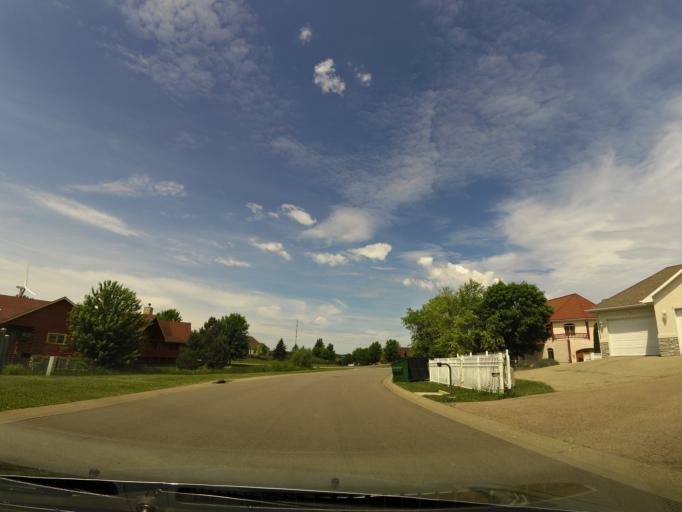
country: US
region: Minnesota
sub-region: Scott County
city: Prior Lake
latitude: 44.7394
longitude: -93.4776
